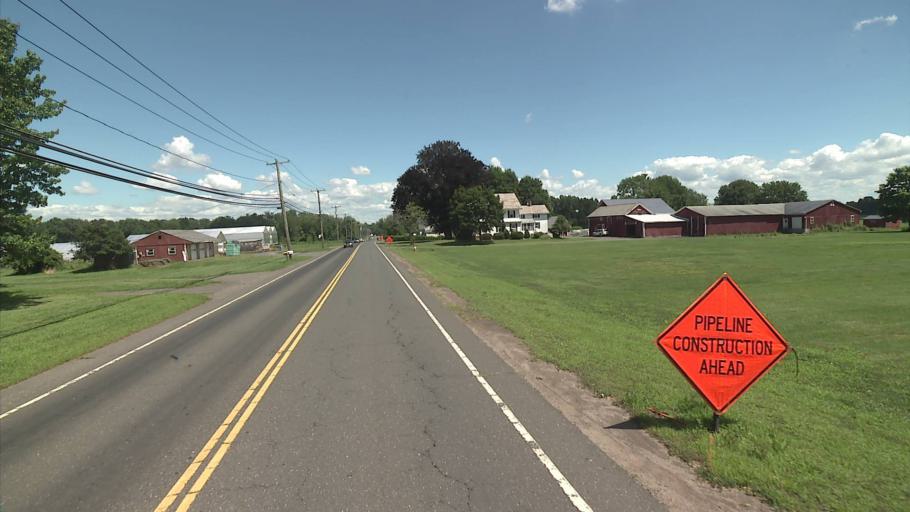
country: US
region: Connecticut
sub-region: Hartford County
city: Suffield Depot
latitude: 41.9831
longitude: -72.6739
